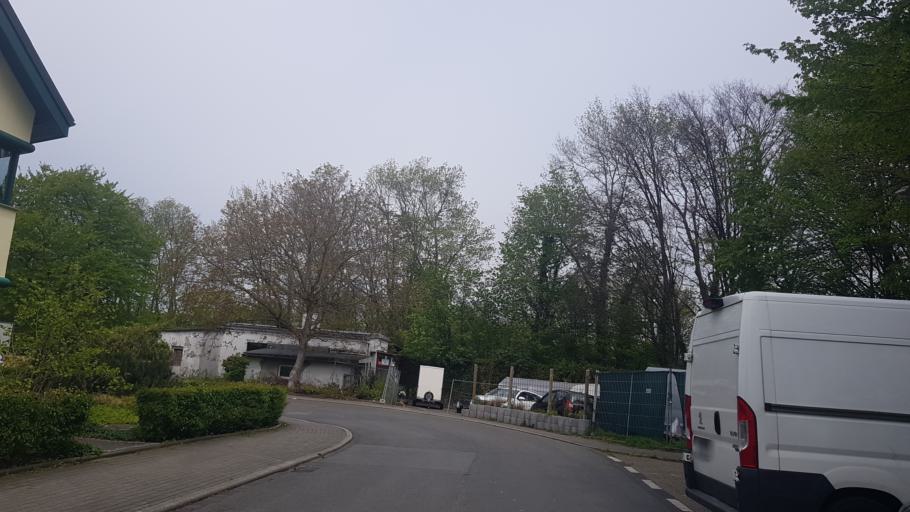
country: DE
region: North Rhine-Westphalia
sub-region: Regierungsbezirk Dusseldorf
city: Oberhausen
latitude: 51.4548
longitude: 6.8973
